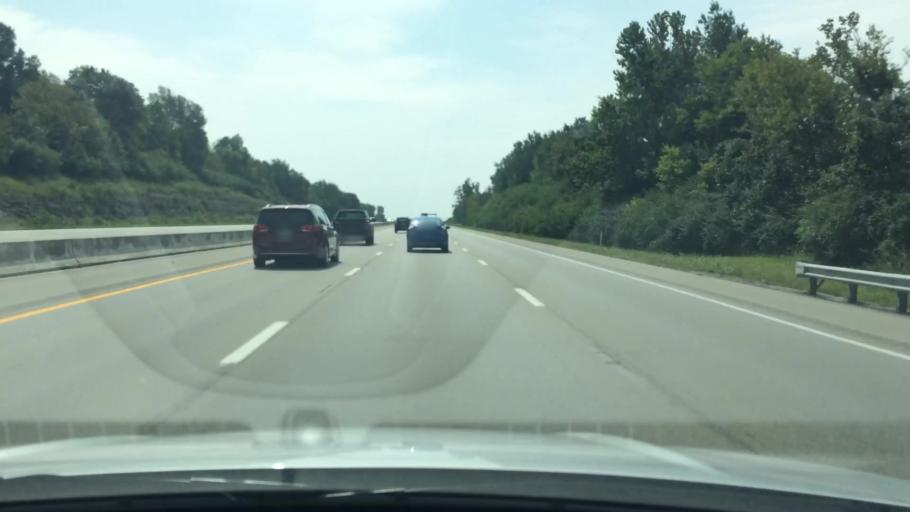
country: US
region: Kentucky
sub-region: Fayette County
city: Lexington
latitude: 37.9485
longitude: -84.3852
